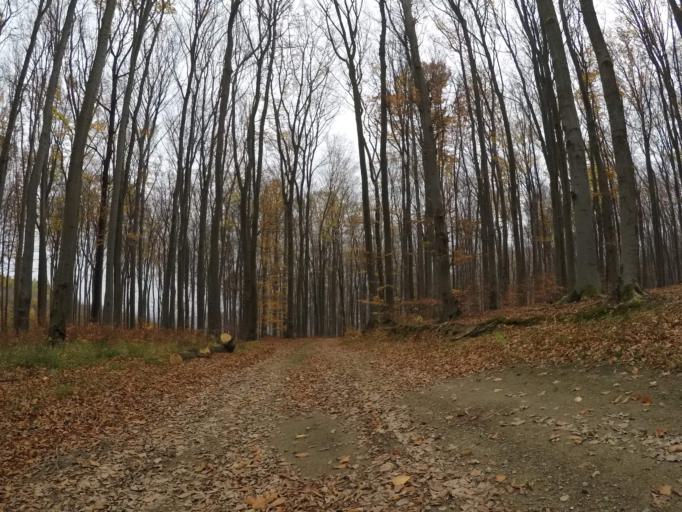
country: SK
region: Presovsky
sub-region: Okres Presov
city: Presov
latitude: 48.8868
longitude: 21.1728
